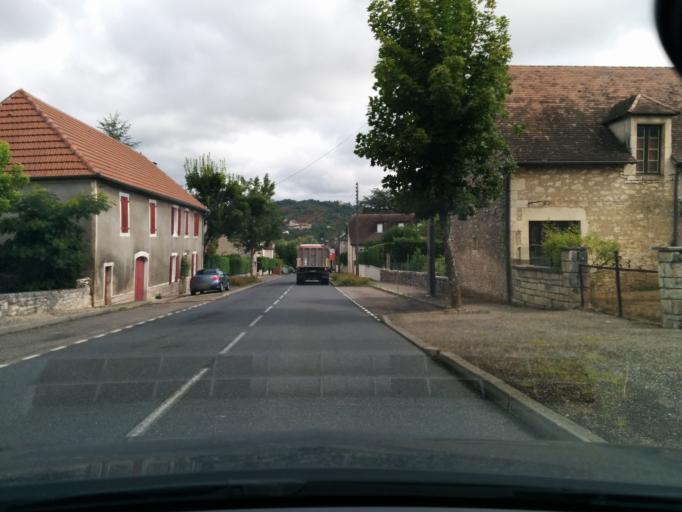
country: FR
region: Midi-Pyrenees
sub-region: Departement du Lot
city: Souillac
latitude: 44.8749
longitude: 1.4834
